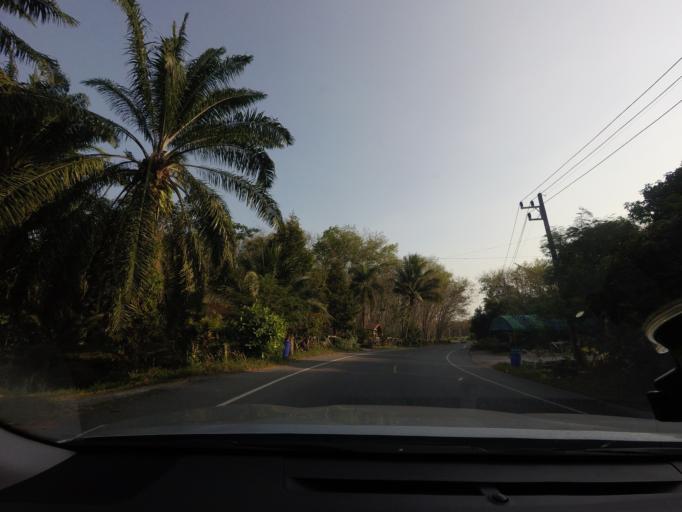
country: TH
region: Surat Thani
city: Phrasaeng
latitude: 8.5724
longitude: 99.2829
